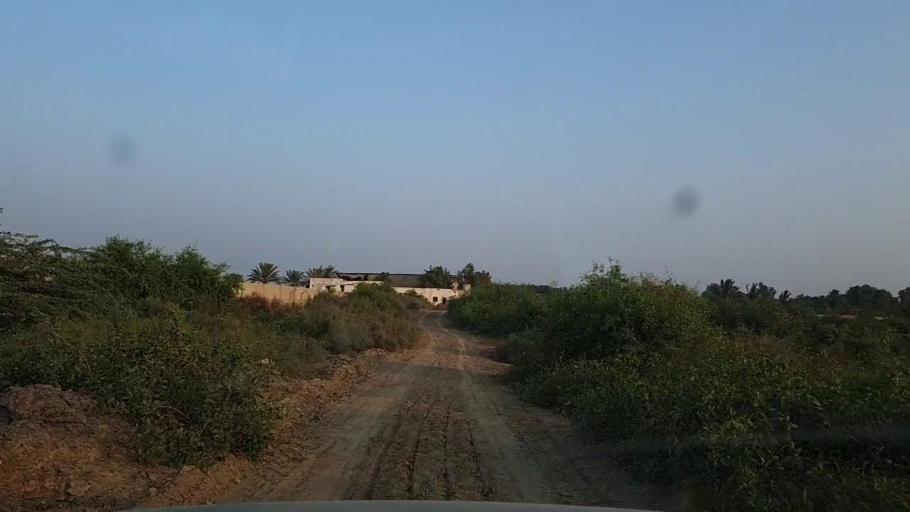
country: PK
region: Sindh
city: Mirpur Sakro
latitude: 24.6133
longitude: 67.5926
